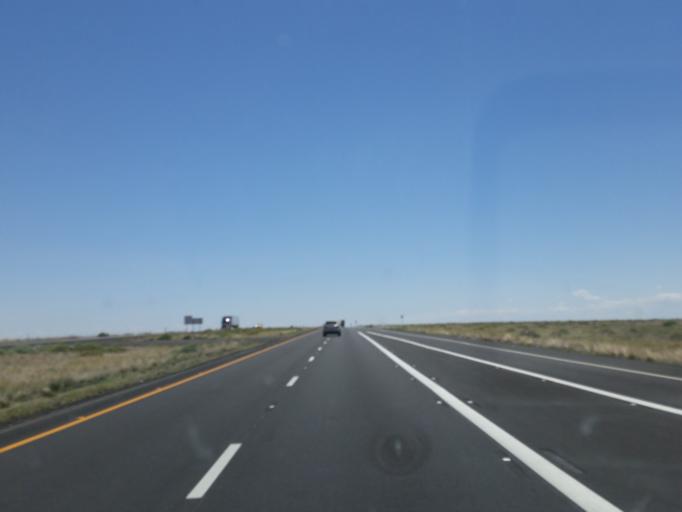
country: US
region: Arizona
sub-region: Coconino County
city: LeChee
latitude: 35.1279
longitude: -111.1811
